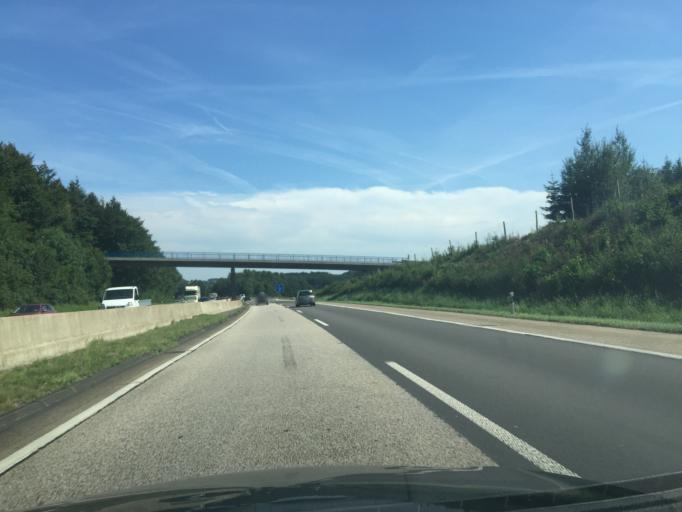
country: DE
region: North Rhine-Westphalia
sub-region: Regierungsbezirk Arnsberg
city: Wenden
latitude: 50.9524
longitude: 7.8546
